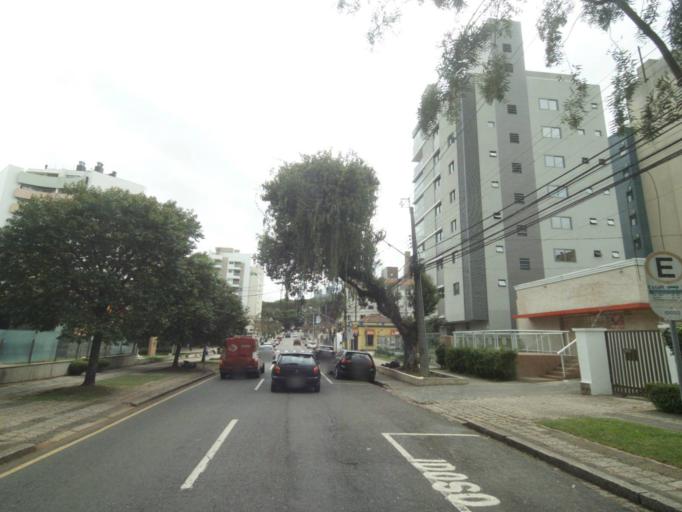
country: BR
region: Parana
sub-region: Curitiba
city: Curitiba
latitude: -25.4336
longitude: -49.2887
